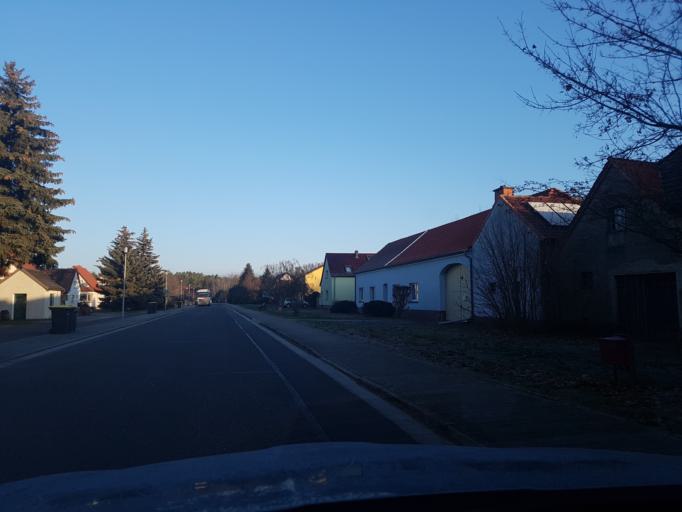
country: DE
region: Brandenburg
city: Schlieben
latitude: 51.6947
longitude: 13.3306
